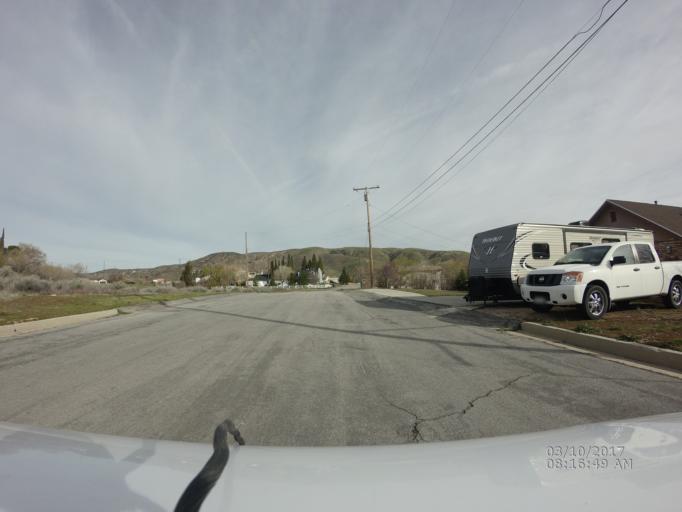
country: US
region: California
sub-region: Los Angeles County
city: Green Valley
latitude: 34.6601
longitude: -118.4010
